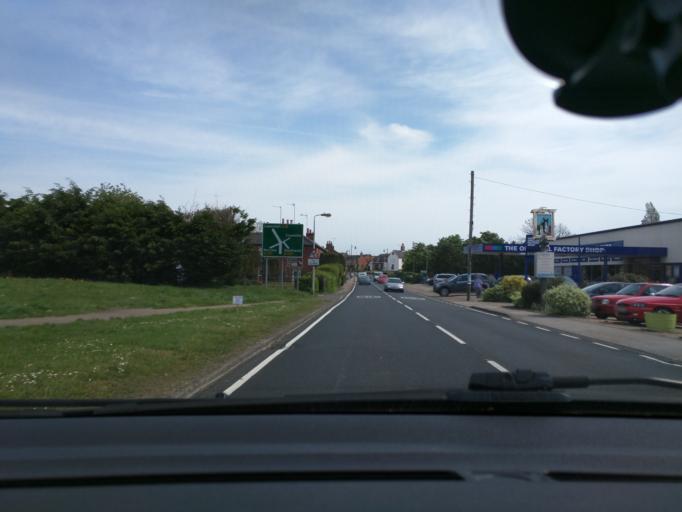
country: GB
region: England
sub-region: Suffolk
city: Wrentham
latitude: 52.3837
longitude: 1.6682
